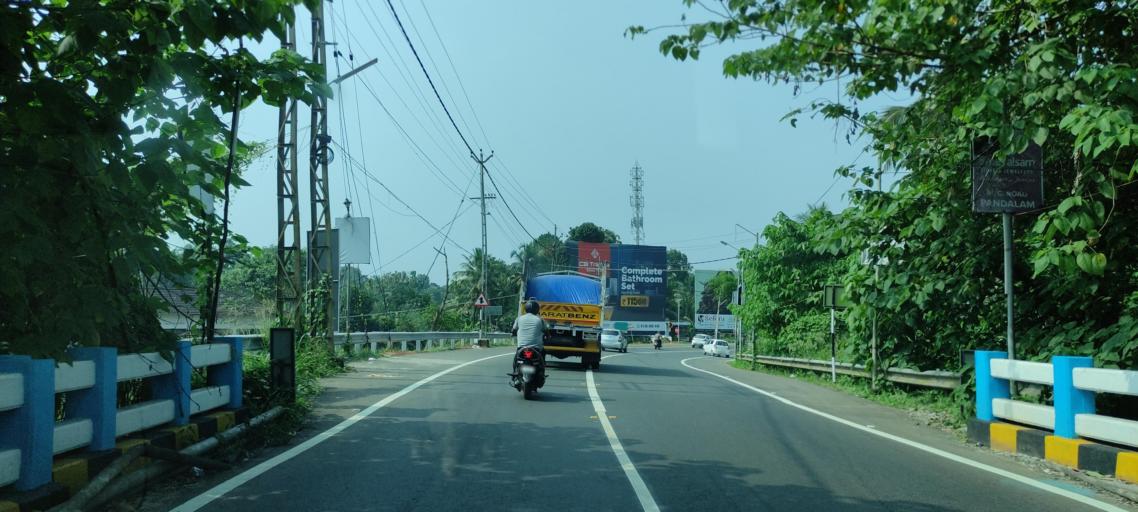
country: IN
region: Kerala
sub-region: Pattanamtitta
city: Adur
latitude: 9.2342
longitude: 76.6730
